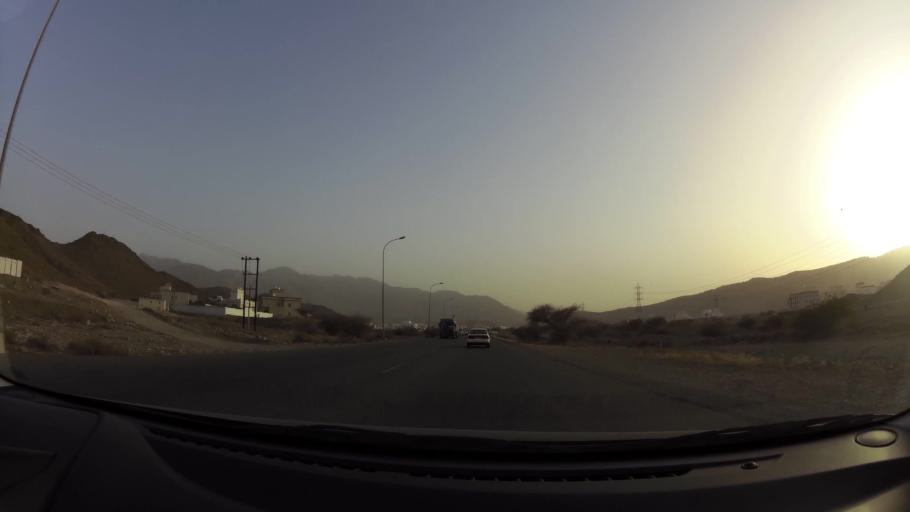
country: OM
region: Muhafazat Masqat
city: Bawshar
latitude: 23.4948
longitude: 58.3224
